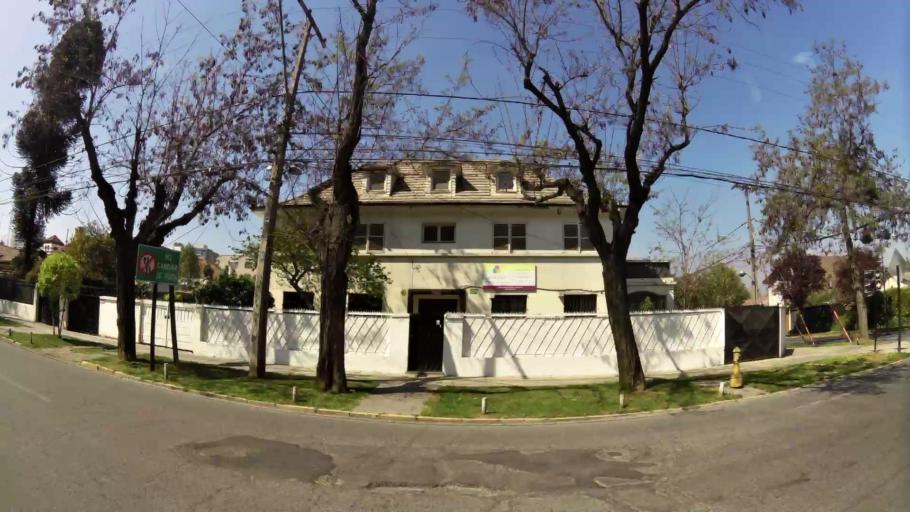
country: CL
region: Santiago Metropolitan
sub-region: Provincia de Santiago
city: Villa Presidente Frei, Nunoa, Santiago, Chile
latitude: -33.4567
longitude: -70.5802
